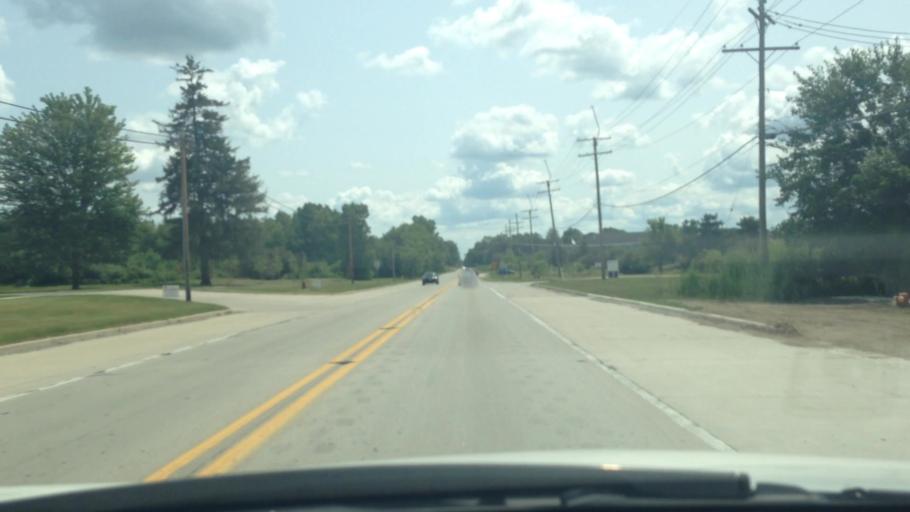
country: US
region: Michigan
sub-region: Wayne County
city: Taylor
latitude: 42.2348
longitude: -83.3079
